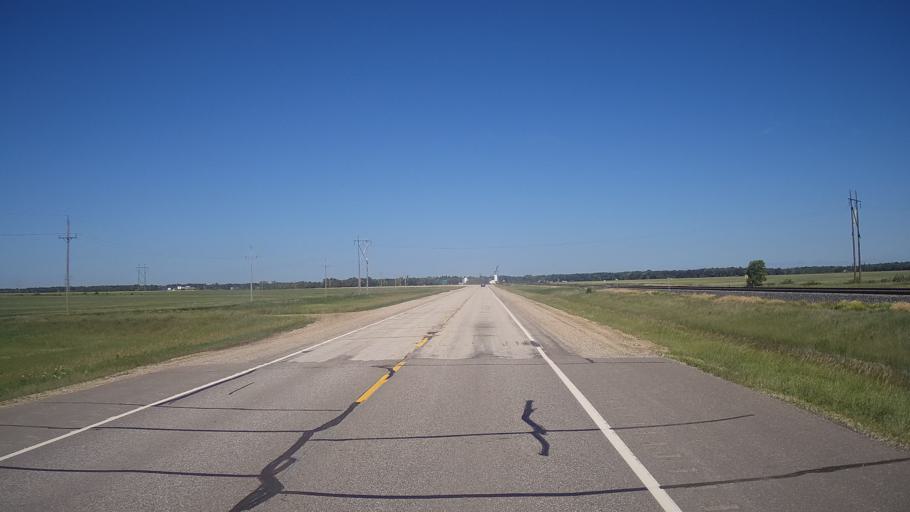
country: CA
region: Manitoba
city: Portage la Prairie
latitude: 50.1210
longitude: -98.5636
